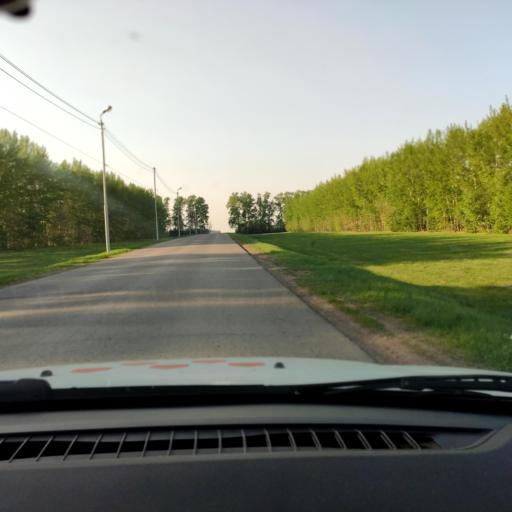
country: RU
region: Bashkortostan
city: Karmaskaly
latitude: 54.3812
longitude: 56.1517
